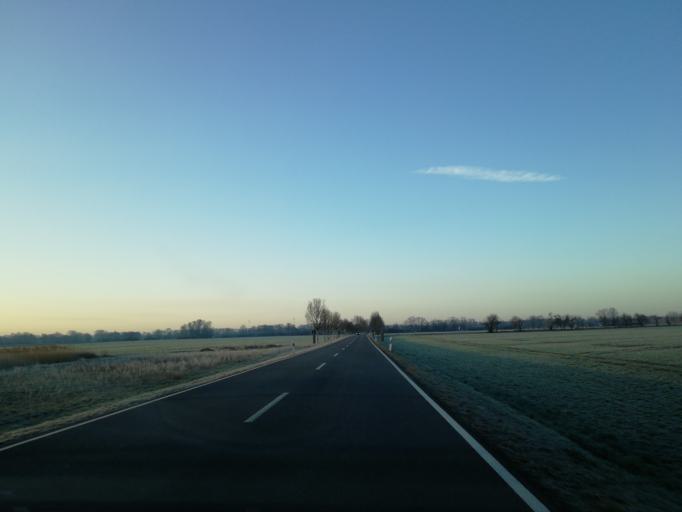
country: DE
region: Brandenburg
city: Finsterwalde
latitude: 51.6821
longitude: 13.7218
